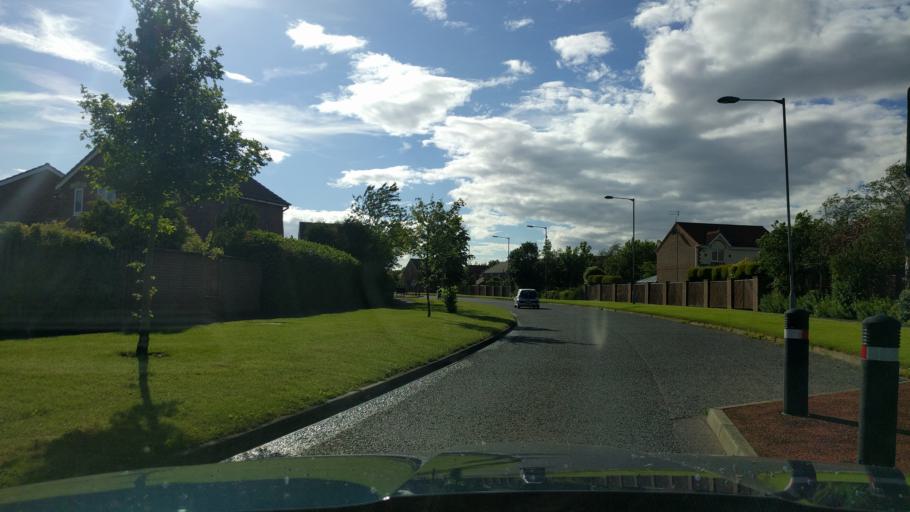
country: GB
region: England
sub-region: Northumberland
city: Cramlington
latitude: 55.1017
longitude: -1.5779
